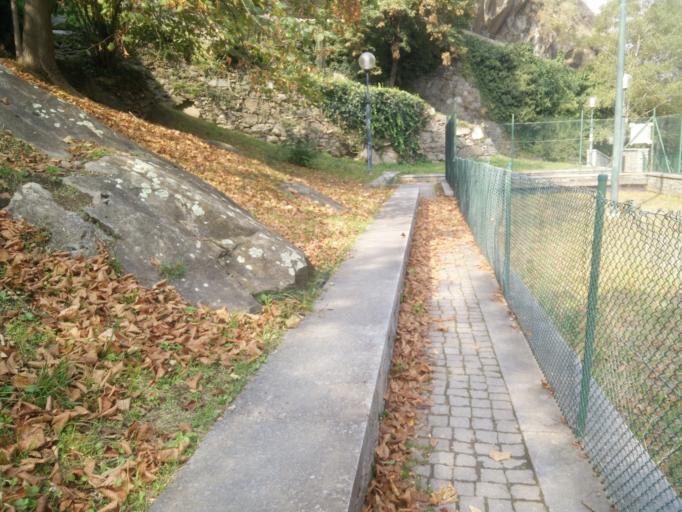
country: IT
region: Aosta Valley
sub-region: Valle d'Aosta
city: Bard
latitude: 45.6068
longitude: 7.7470
